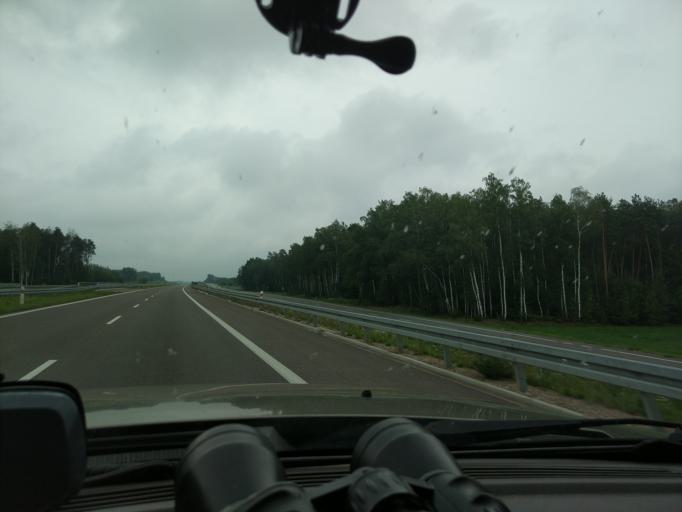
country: PL
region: Podlasie
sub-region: Powiat zambrowski
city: Rutki-Kossaki
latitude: 53.0656
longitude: 22.4125
